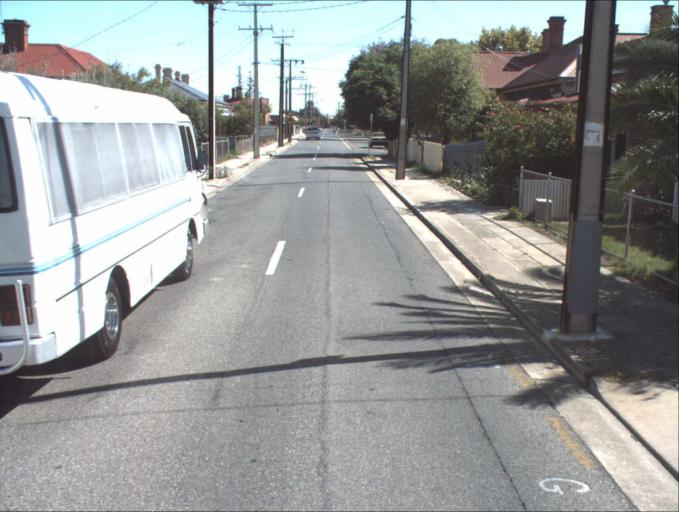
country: AU
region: South Australia
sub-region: Port Adelaide Enfield
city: Alberton
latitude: -34.8555
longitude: 138.5193
